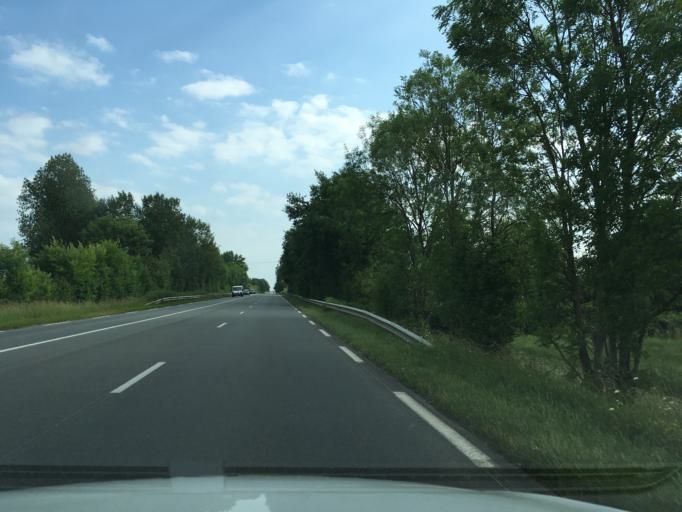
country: FR
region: Poitou-Charentes
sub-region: Departement des Deux-Sevres
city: Le Tallud
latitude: 46.6080
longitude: -0.2860
